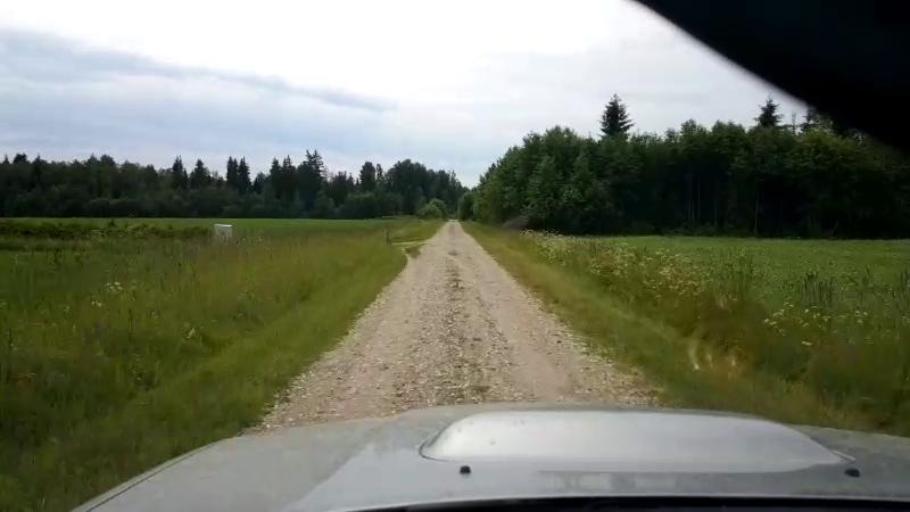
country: EE
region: Paernumaa
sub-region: Tootsi vald
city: Tootsi
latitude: 58.5568
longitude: 24.7494
